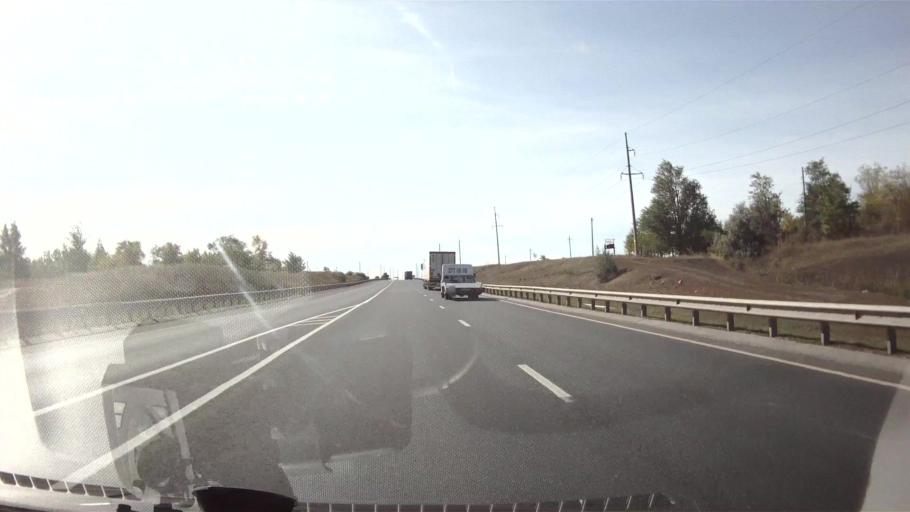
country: RU
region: Samara
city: Varlamovo
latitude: 53.2017
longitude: 48.3787
